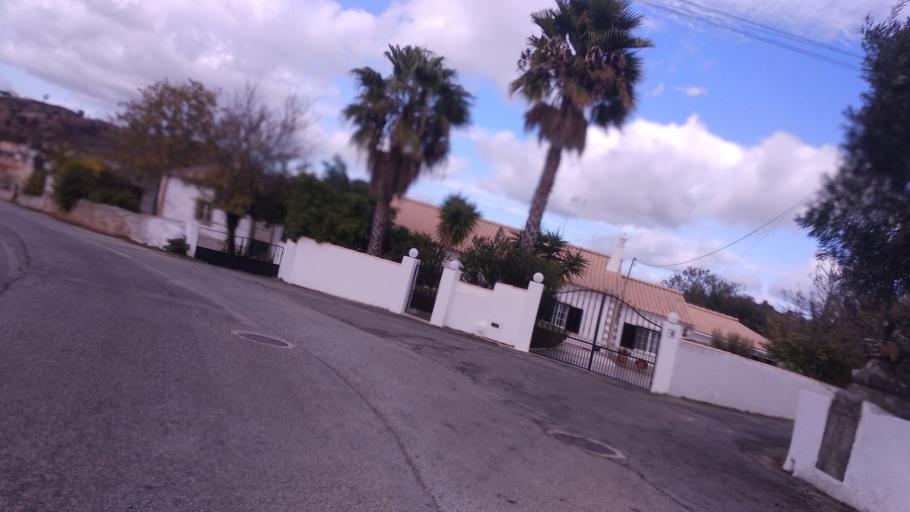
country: PT
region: Faro
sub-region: Sao Bras de Alportel
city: Sao Bras de Alportel
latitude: 37.1712
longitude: -7.8948
